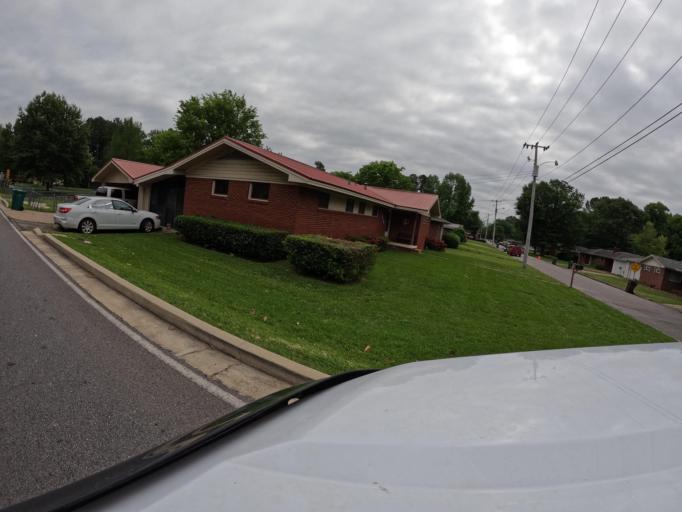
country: US
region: Mississippi
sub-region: Lee County
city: Tupelo
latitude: 34.2670
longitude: -88.7377
